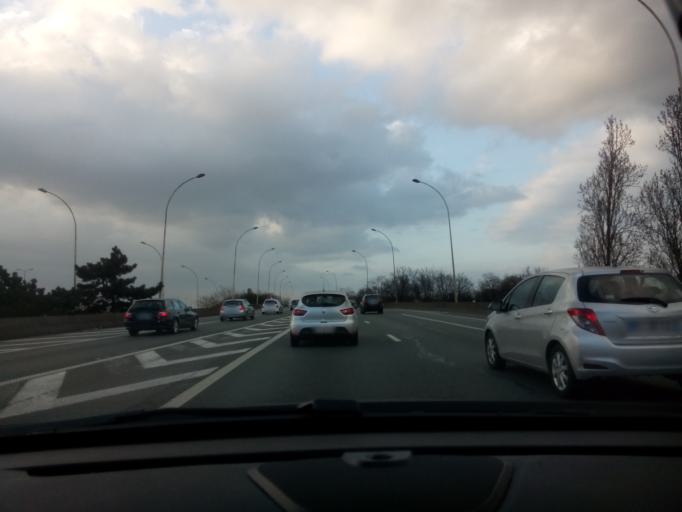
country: FR
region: Ile-de-France
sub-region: Departement du Val-de-Marne
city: L'Hay-les-Roses
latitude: 48.7854
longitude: 2.3466
